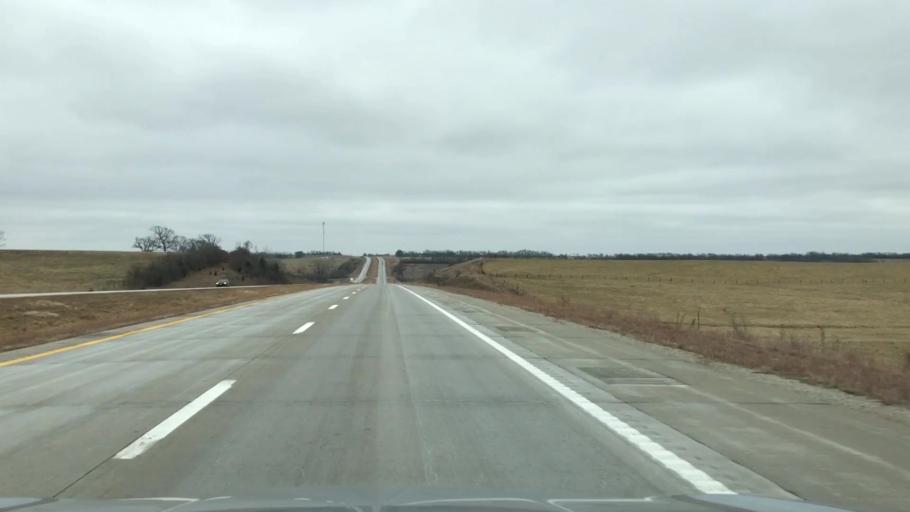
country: US
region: Missouri
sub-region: Caldwell County
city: Hamilton
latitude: 39.7348
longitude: -93.7900
